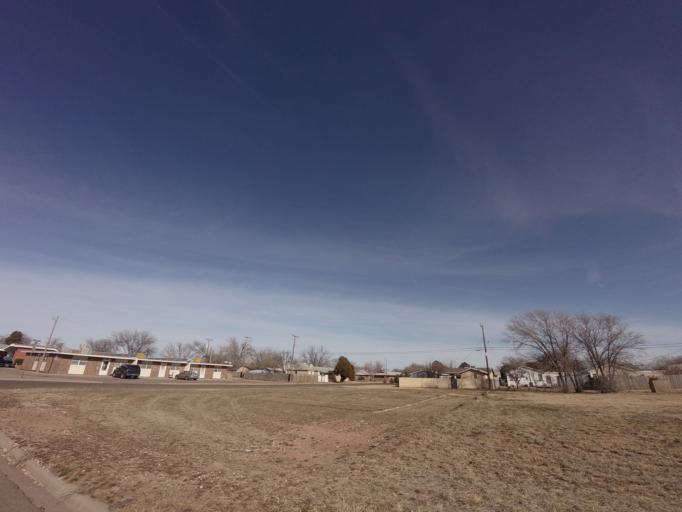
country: US
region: New Mexico
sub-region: Curry County
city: Clovis
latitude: 34.4096
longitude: -103.2229
